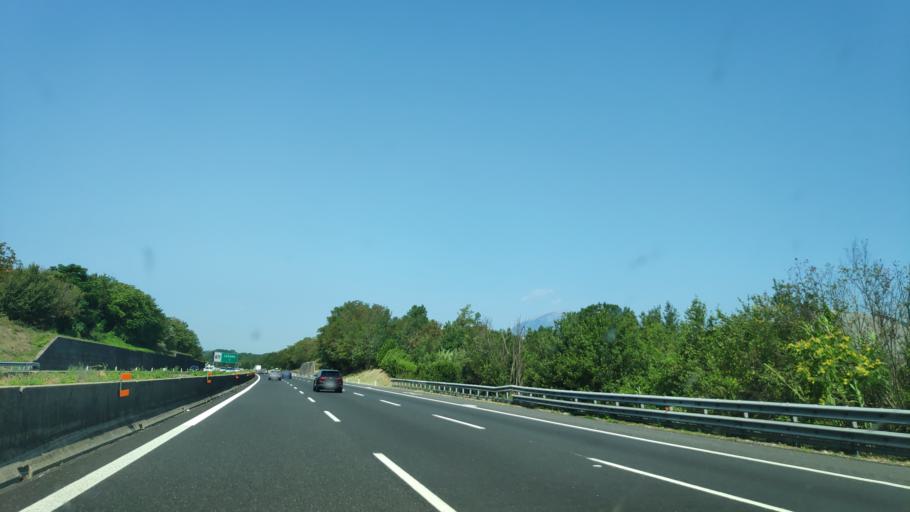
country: IT
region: Latium
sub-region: Provincia di Frosinone
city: Sant'Ambrogio sul Garigliano
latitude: 41.4402
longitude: 13.8789
